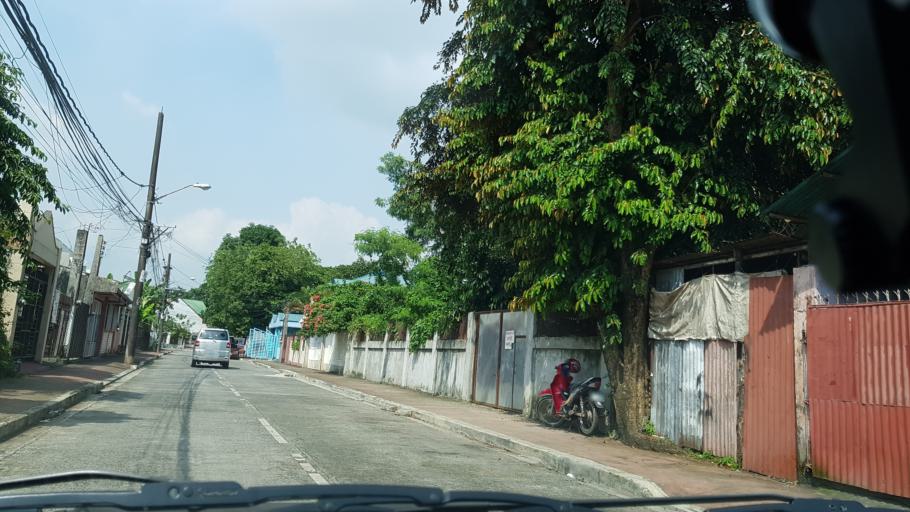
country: PH
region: Calabarzon
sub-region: Province of Rizal
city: San Mateo
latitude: 14.6646
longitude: 121.1121
